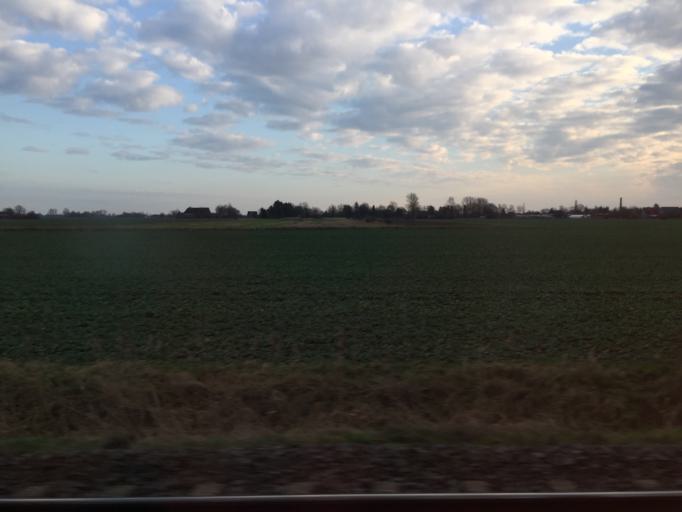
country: DE
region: Schleswig-Holstein
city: Blomesche Wildnis
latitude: 53.8053
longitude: 9.4342
